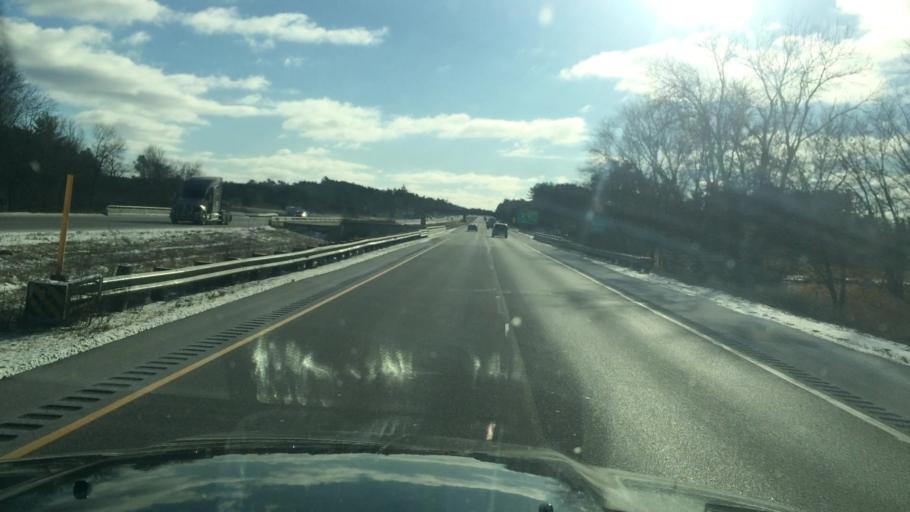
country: US
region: Wisconsin
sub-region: Portage County
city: Stevens Point
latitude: 44.5277
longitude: -89.5318
